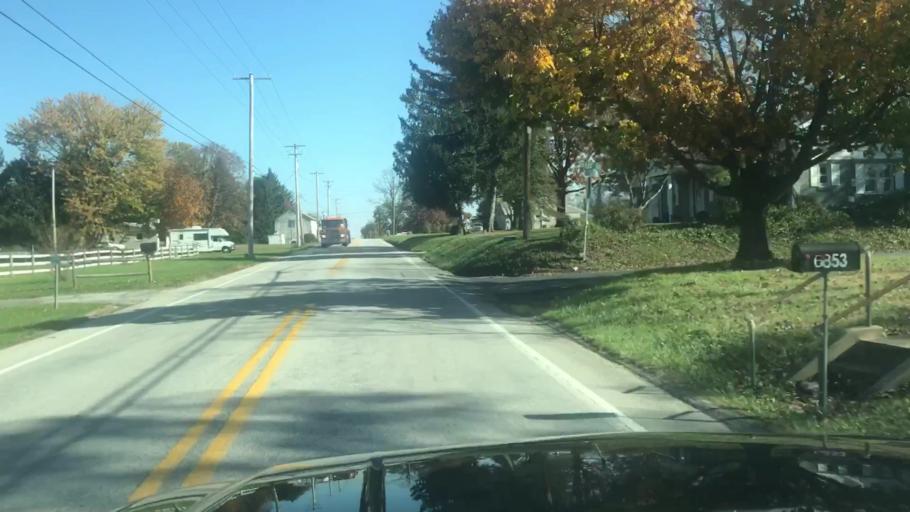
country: US
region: Pennsylvania
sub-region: Cumberland County
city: Mechanicsburg
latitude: 40.2857
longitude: -77.0211
